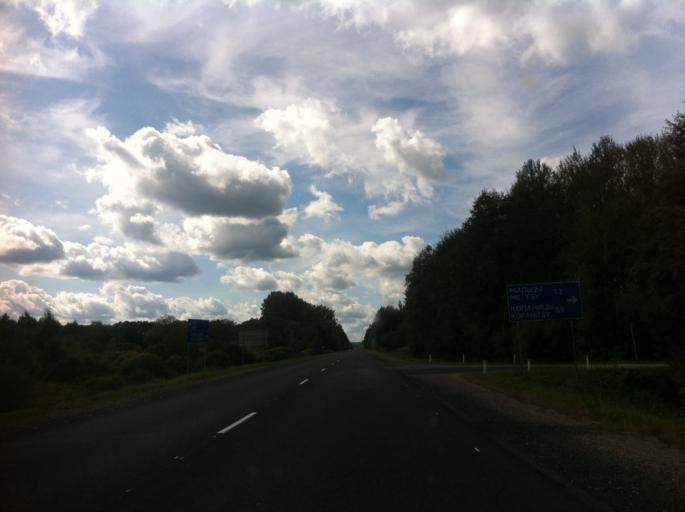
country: RU
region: Pskov
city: Izborsk
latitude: 57.7133
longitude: 27.9062
